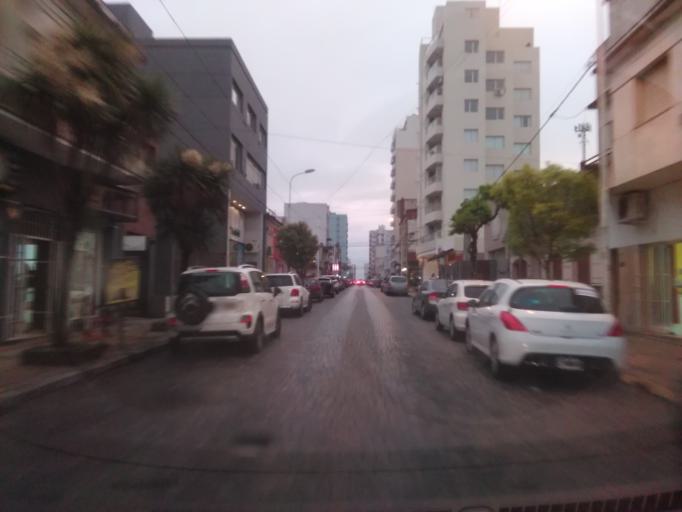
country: AR
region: Buenos Aires
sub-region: Partido de Tandil
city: Tandil
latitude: -37.3264
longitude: -59.1407
